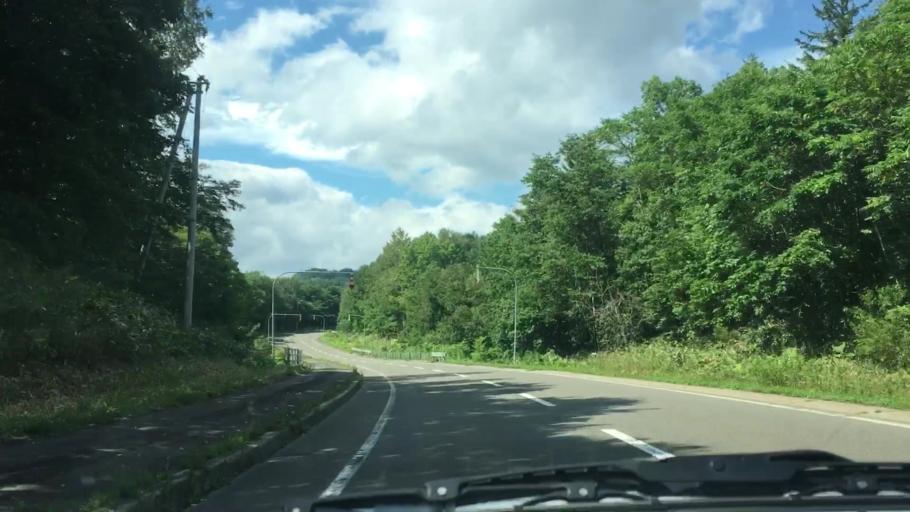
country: JP
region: Hokkaido
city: Otofuke
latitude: 43.3397
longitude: 143.2859
